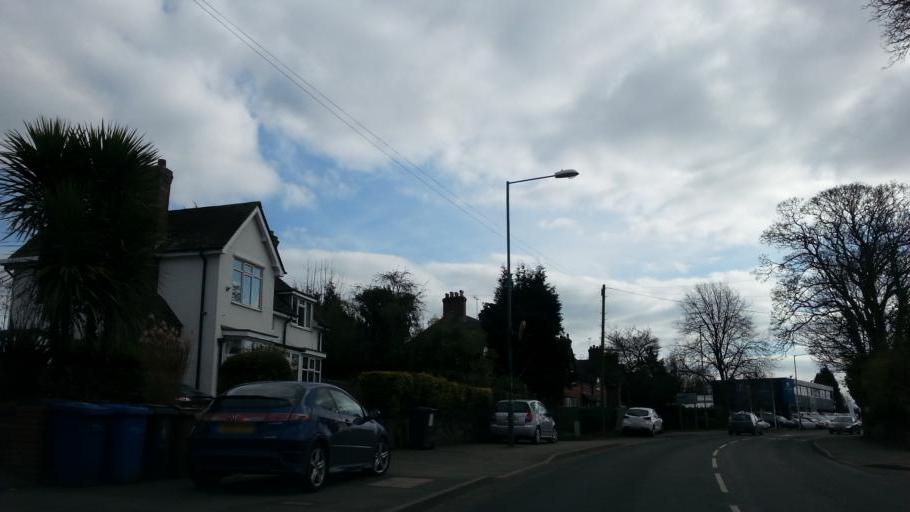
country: GB
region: England
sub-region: Staffordshire
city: Lichfield
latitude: 52.6752
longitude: -1.8309
